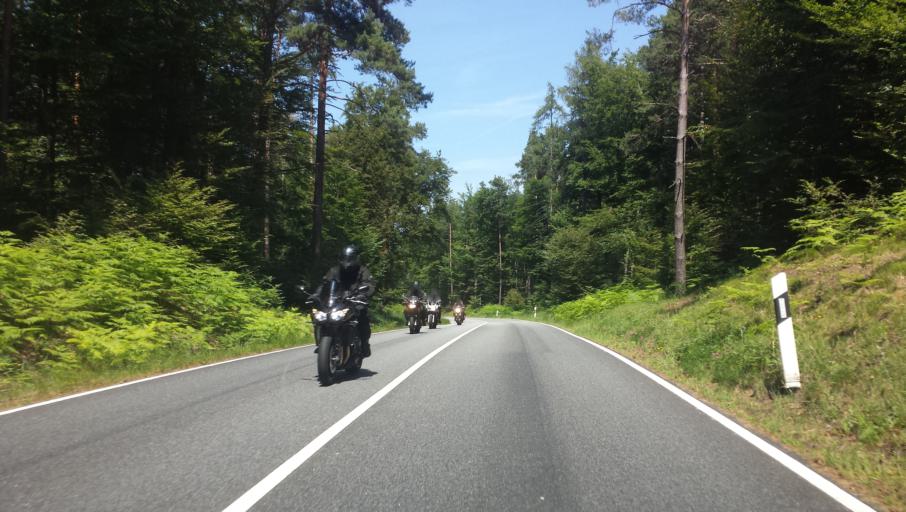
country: DE
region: Rheinland-Pfalz
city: Waldleiningen
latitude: 49.4172
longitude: 7.8826
